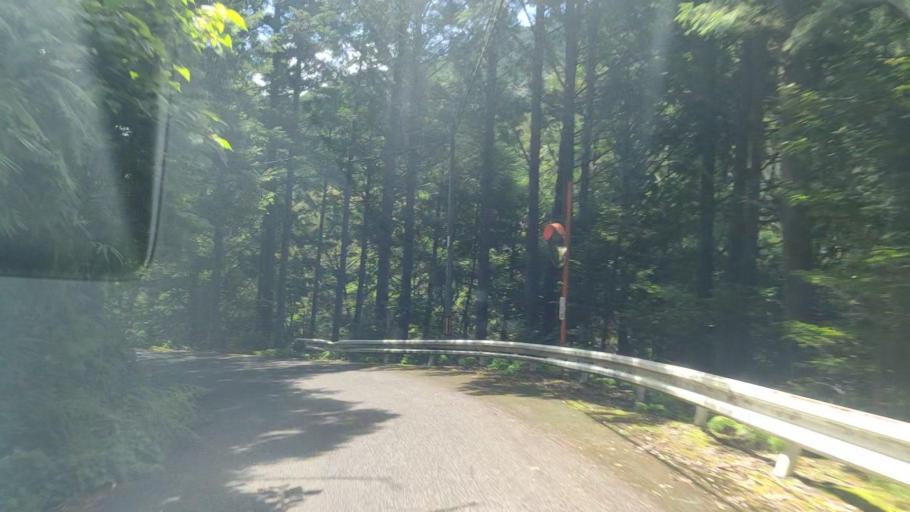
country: JP
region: Wakayama
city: Shingu
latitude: 33.9066
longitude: 135.8678
